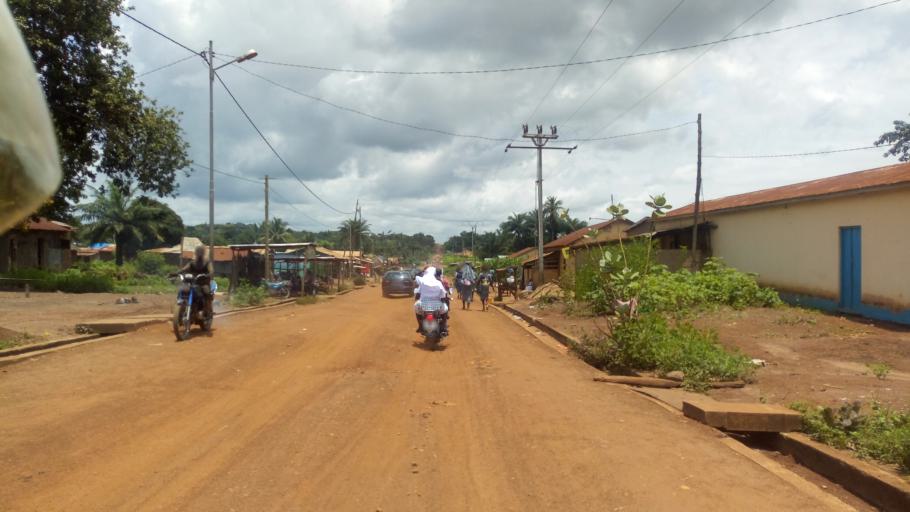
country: TG
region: Centrale
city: Sotouboua
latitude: 8.4336
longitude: 0.9923
